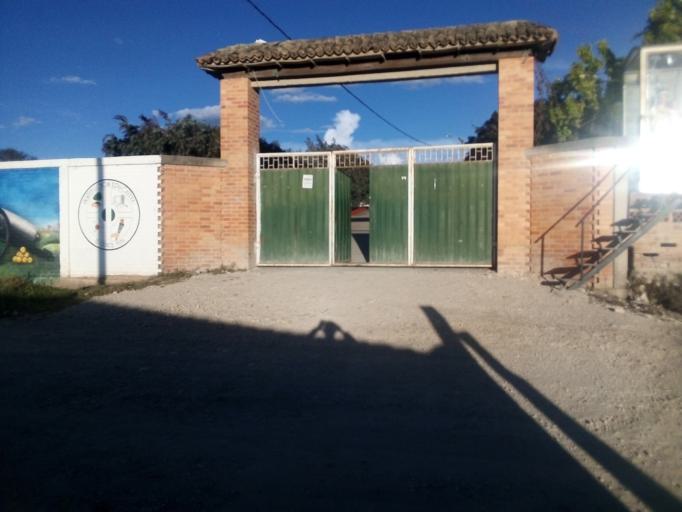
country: CO
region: Boyaca
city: Tuta
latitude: 5.6596
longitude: -73.1513
